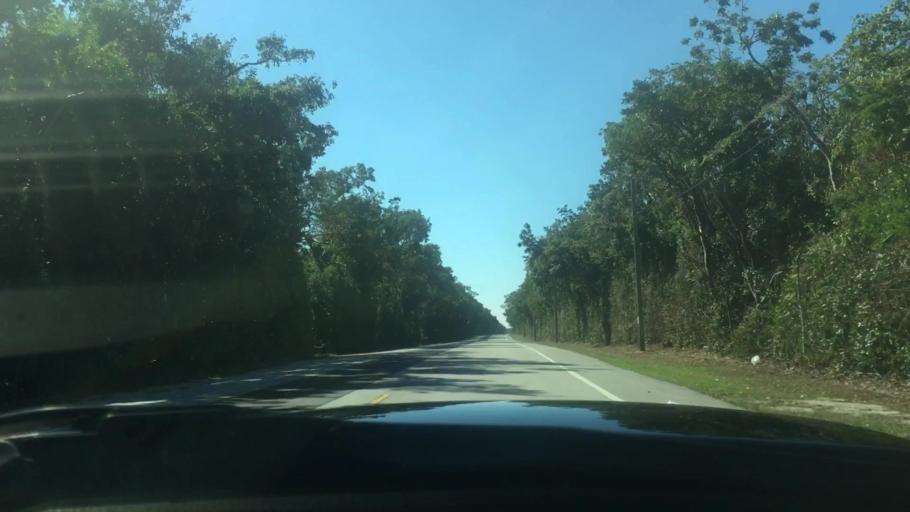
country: US
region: Florida
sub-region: Monroe County
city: North Key Largo
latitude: 25.2455
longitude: -80.3194
